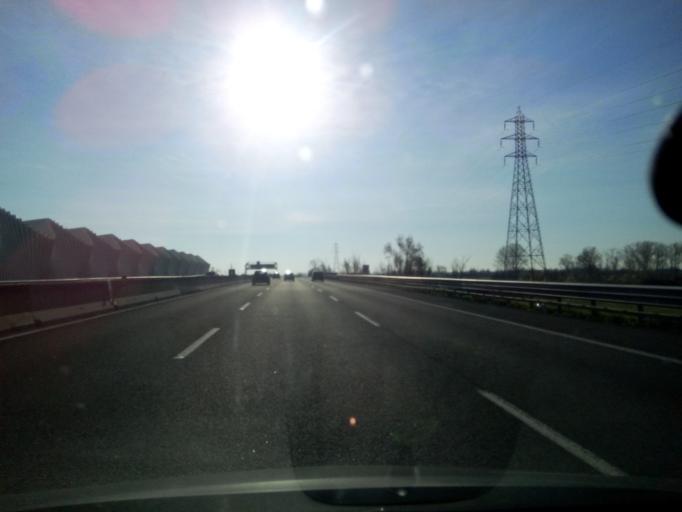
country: IT
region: Emilia-Romagna
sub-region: Provincia di Reggio Emilia
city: Reggio nell'Emilia
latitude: 44.7240
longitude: 10.6530
